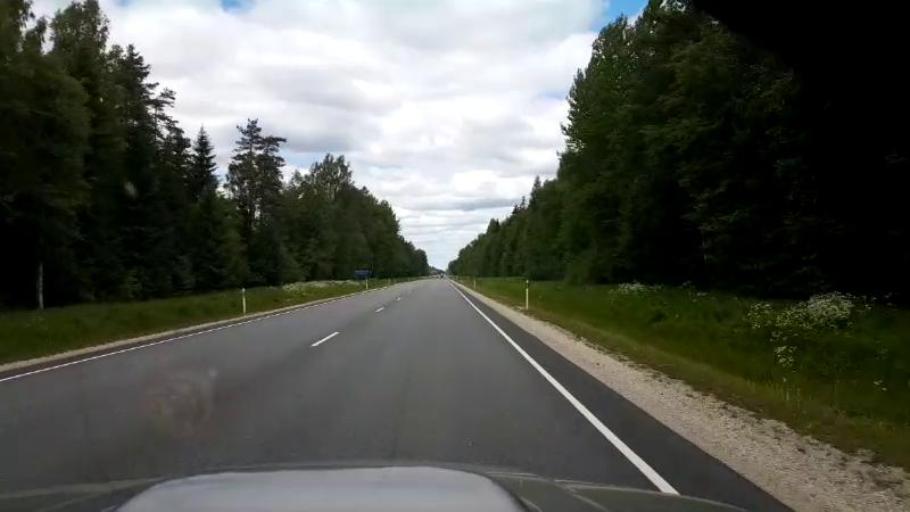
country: EE
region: Raplamaa
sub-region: Maerjamaa vald
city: Marjamaa
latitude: 58.7936
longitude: 24.4129
